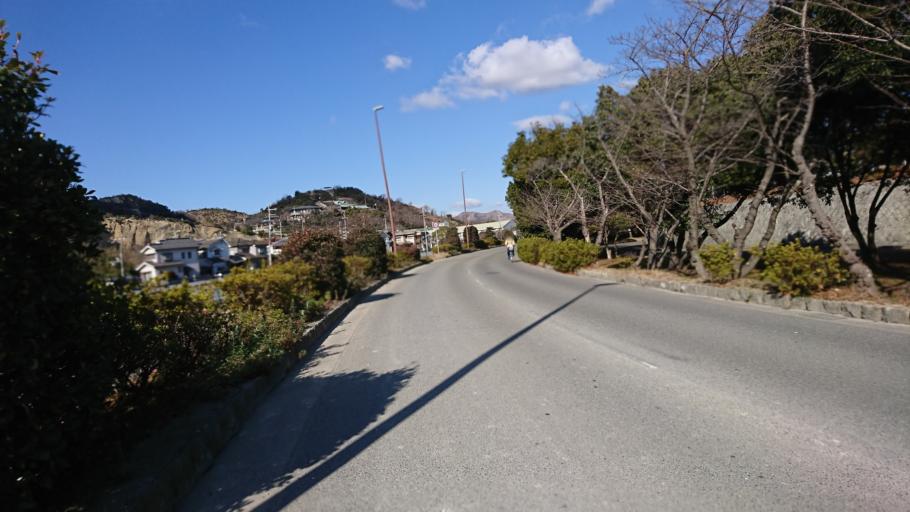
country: JP
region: Hyogo
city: Kakogawacho-honmachi
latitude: 34.7796
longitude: 134.7982
